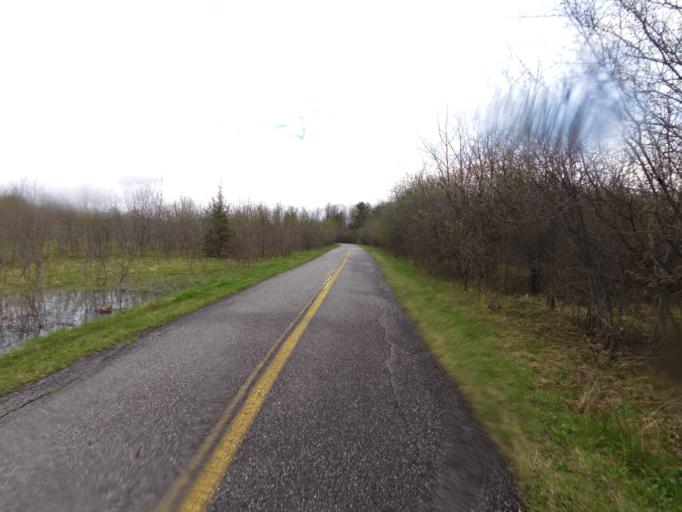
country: CA
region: Quebec
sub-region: Outaouais
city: Gatineau
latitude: 45.4430
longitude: -75.7599
